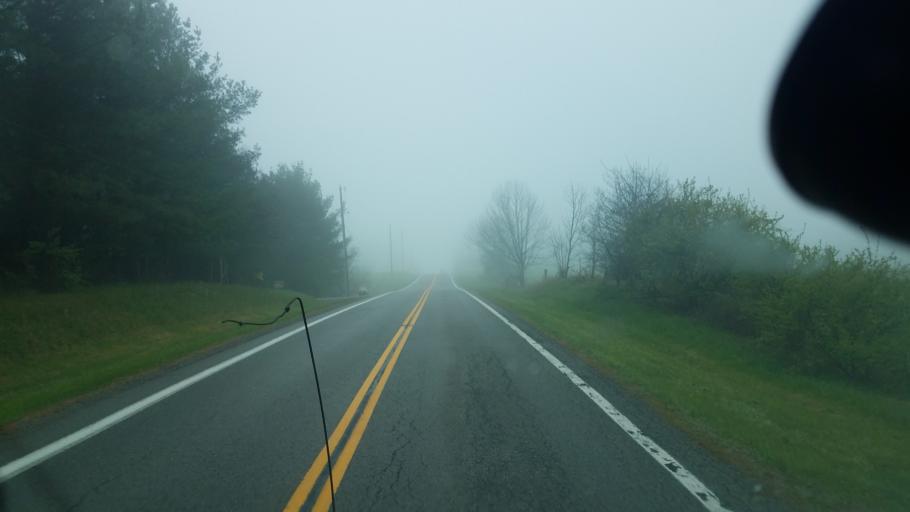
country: US
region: Ohio
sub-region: Logan County
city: Bellefontaine
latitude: 40.3963
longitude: -83.6919
